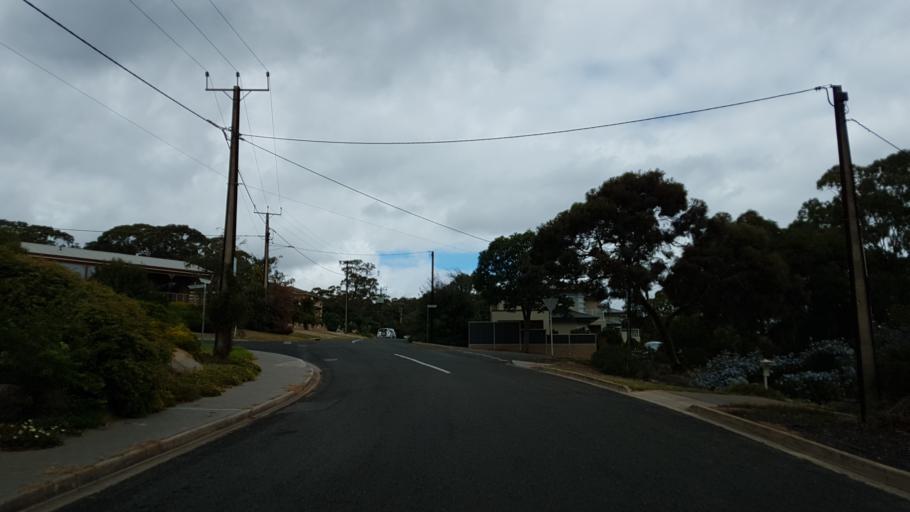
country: AU
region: South Australia
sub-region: Mitcham
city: Clapham
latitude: -35.0060
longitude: 138.5938
